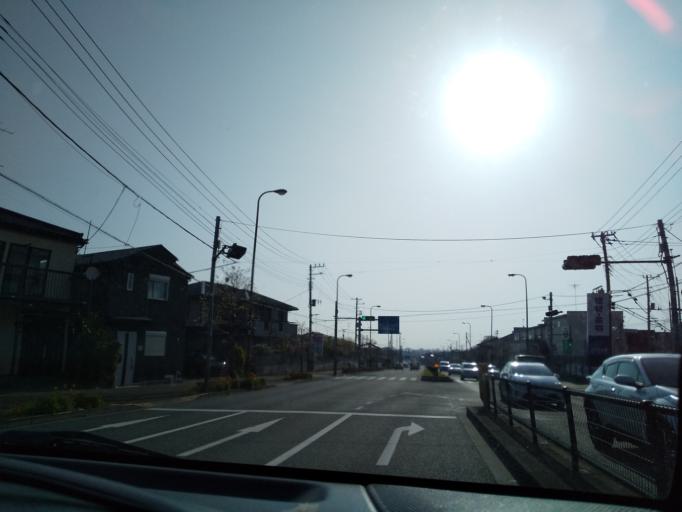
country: JP
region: Tokyo
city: Fussa
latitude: 35.7393
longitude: 139.2861
